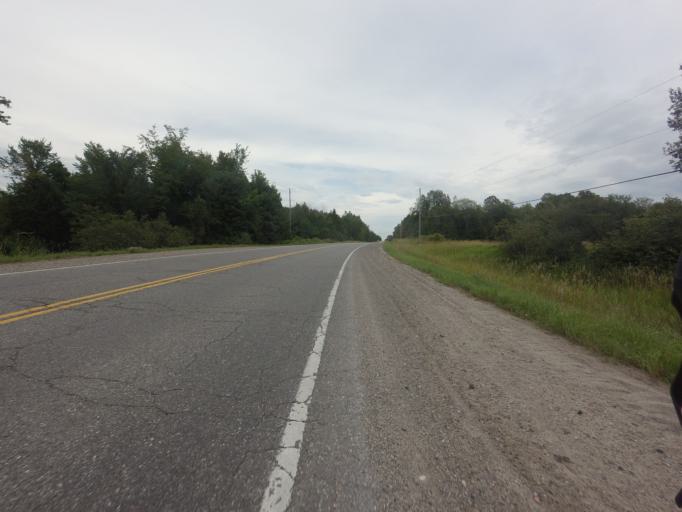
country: CA
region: Ontario
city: Carleton Place
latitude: 45.1403
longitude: -76.3268
